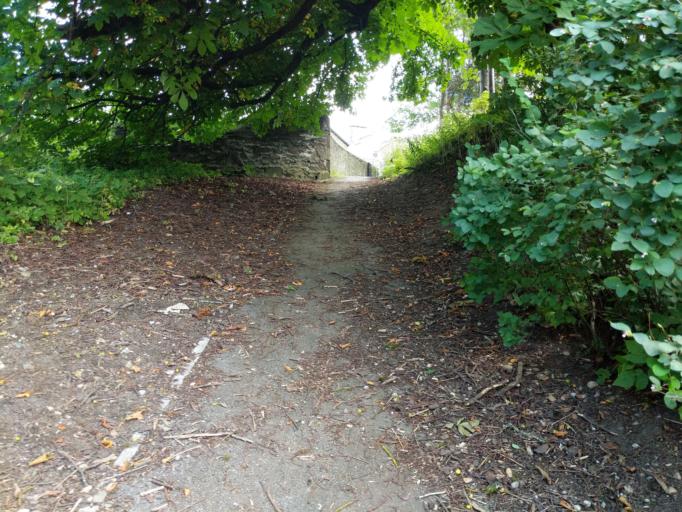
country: GB
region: Scotland
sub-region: Moray
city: Keith
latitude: 57.5441
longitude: -2.9539
